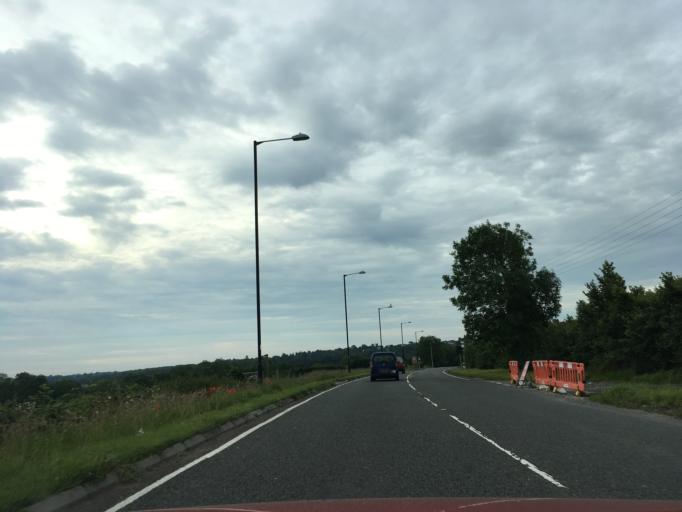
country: GB
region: England
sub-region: North Somerset
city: Easton-in-Gordano
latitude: 51.4704
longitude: -2.6839
